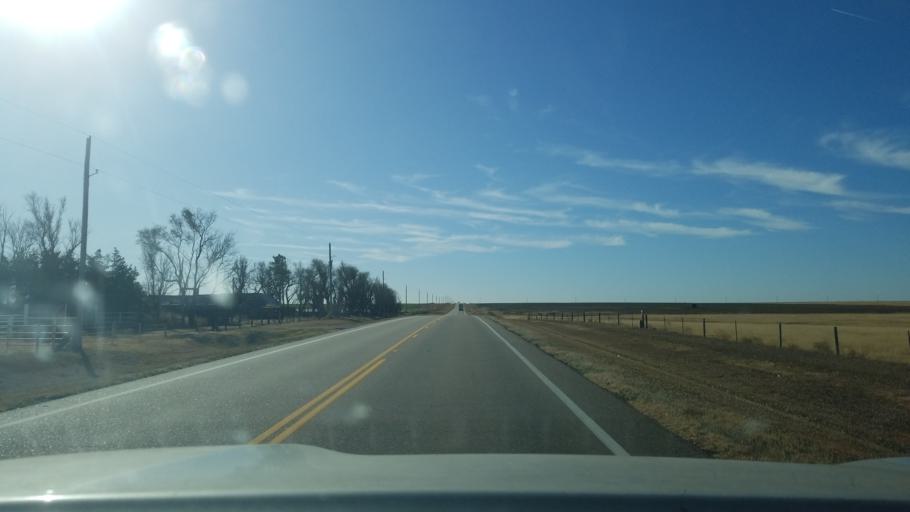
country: US
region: Kansas
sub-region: Ness County
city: Ness City
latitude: 38.4029
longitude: -99.8984
